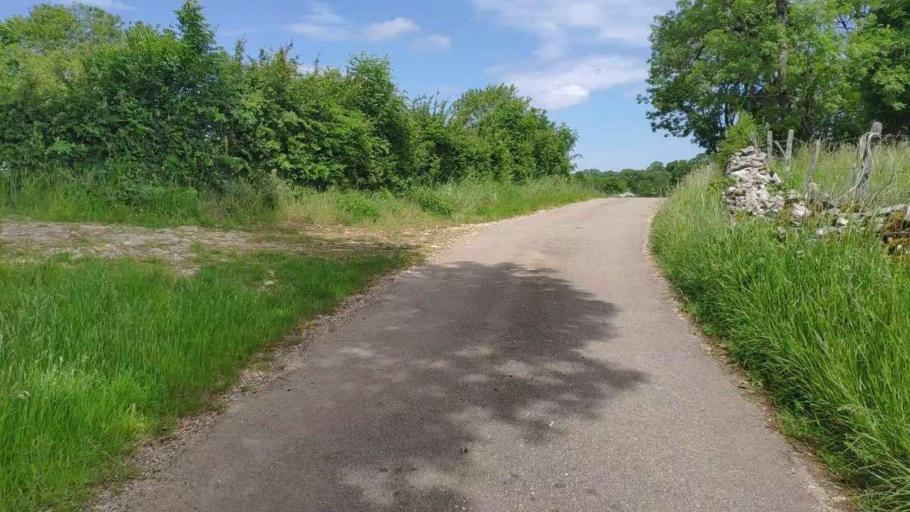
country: FR
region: Franche-Comte
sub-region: Departement du Jura
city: Perrigny
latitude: 46.7503
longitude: 5.6360
